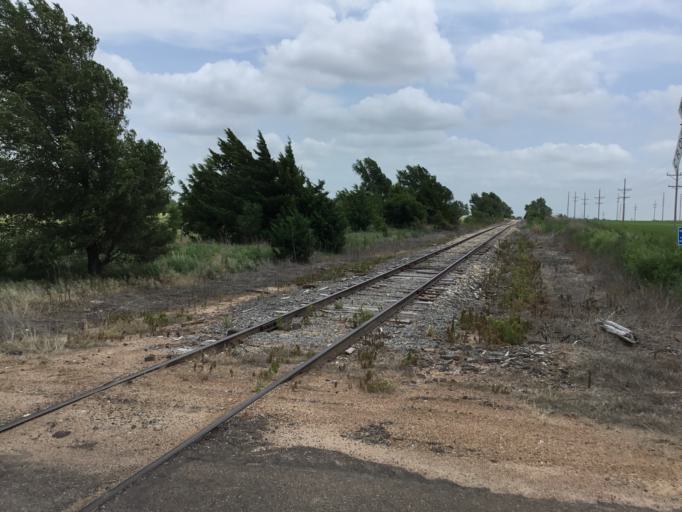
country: US
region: Kansas
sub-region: Pratt County
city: Pratt
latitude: 37.6468
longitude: -98.4649
